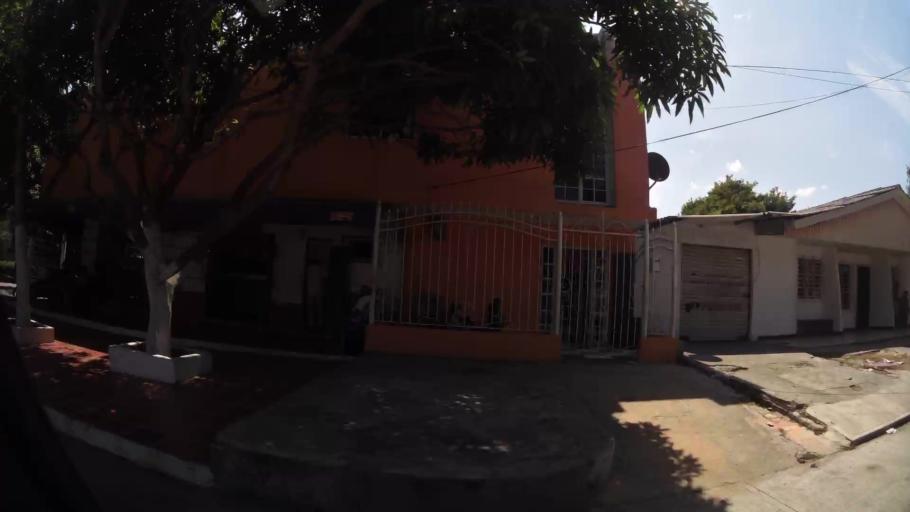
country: CO
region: Atlantico
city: Barranquilla
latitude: 10.9673
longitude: -74.8010
